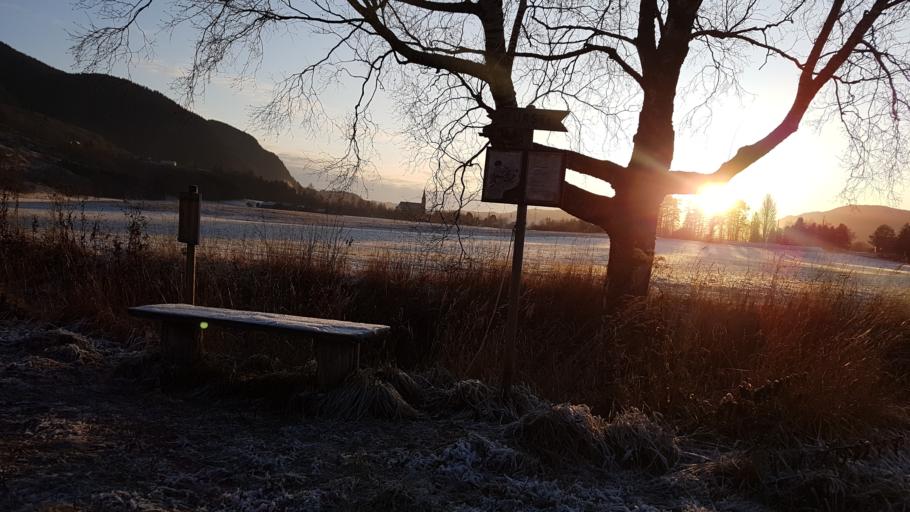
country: NO
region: Sor-Trondelag
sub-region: Melhus
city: Melhus
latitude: 63.2836
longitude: 10.2985
